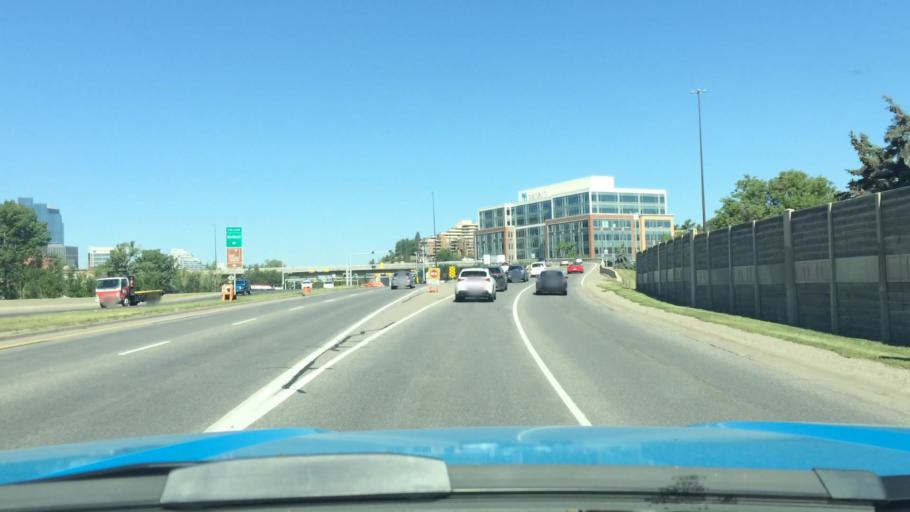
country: CA
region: Alberta
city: Calgary
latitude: 51.0499
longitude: -114.0474
